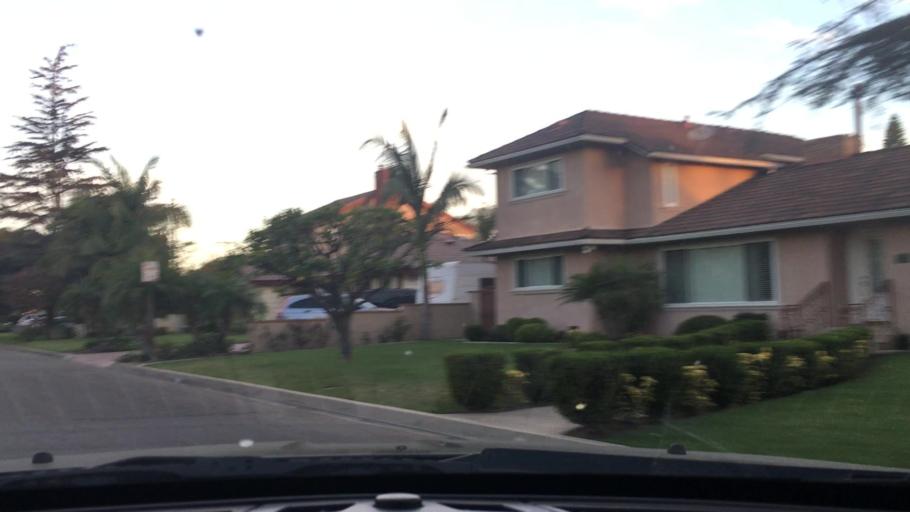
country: US
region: California
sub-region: Los Angeles County
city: Downey
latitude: 33.9503
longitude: -118.1139
